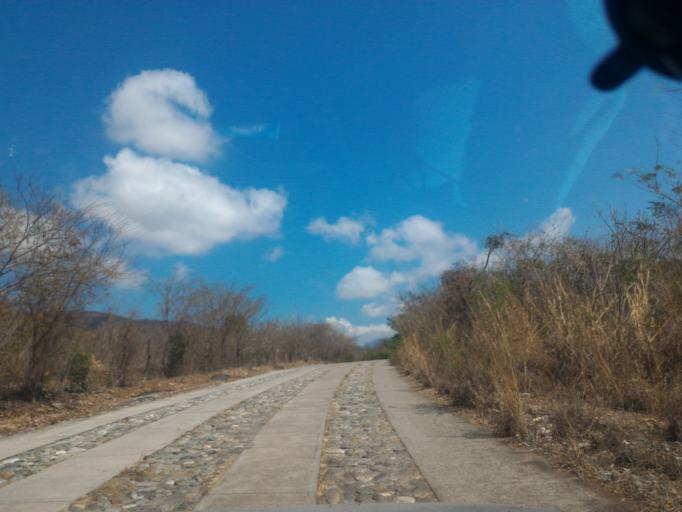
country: MX
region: Michoacan
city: Coahuayana Viejo
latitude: 18.5607
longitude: -103.6377
